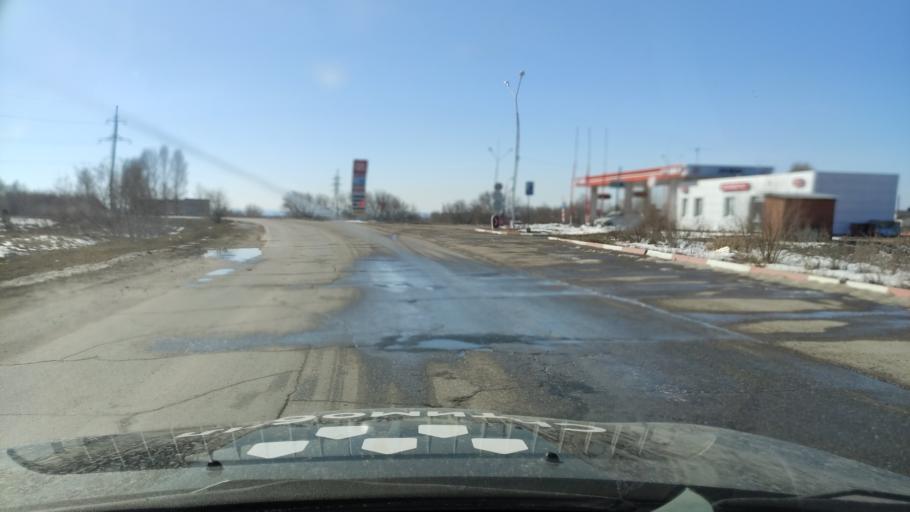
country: RU
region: Samara
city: Povolzhskiy
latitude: 53.5745
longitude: 49.6920
